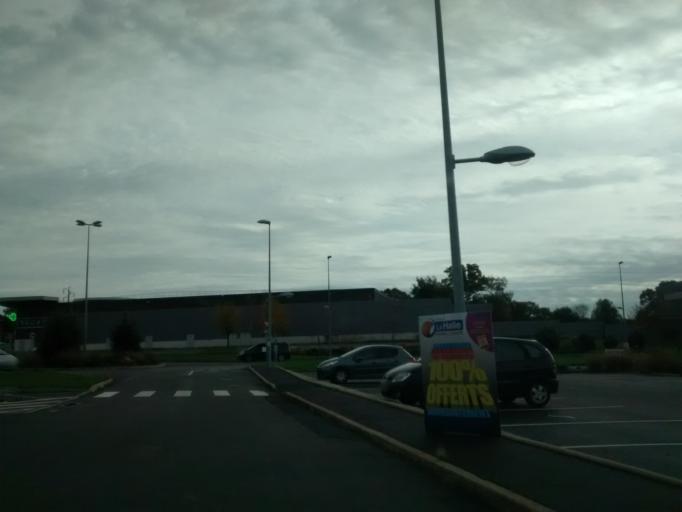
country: FR
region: Brittany
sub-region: Departement d'Ille-et-Vilaine
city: Chantepie
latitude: 48.0632
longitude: -1.6255
